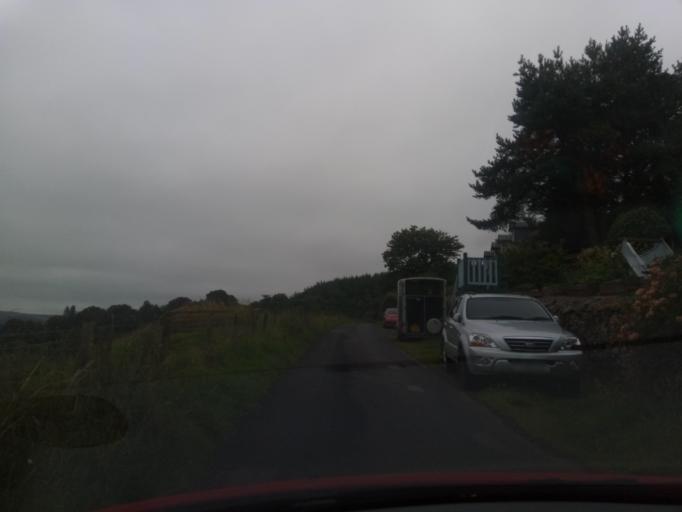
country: GB
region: Scotland
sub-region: Fife
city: Pathhead
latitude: 55.7444
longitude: -2.9233
